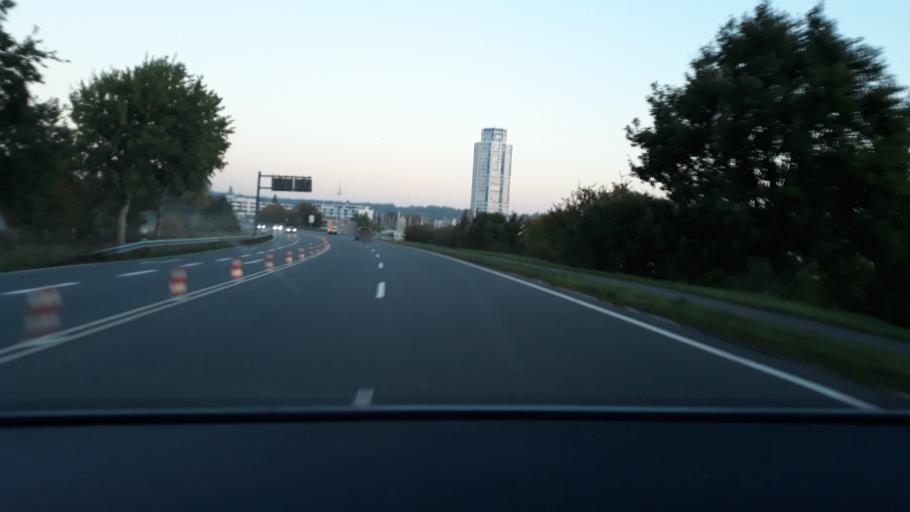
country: DE
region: Schleswig-Holstein
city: Busdorf
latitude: 54.5028
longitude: 9.5525
